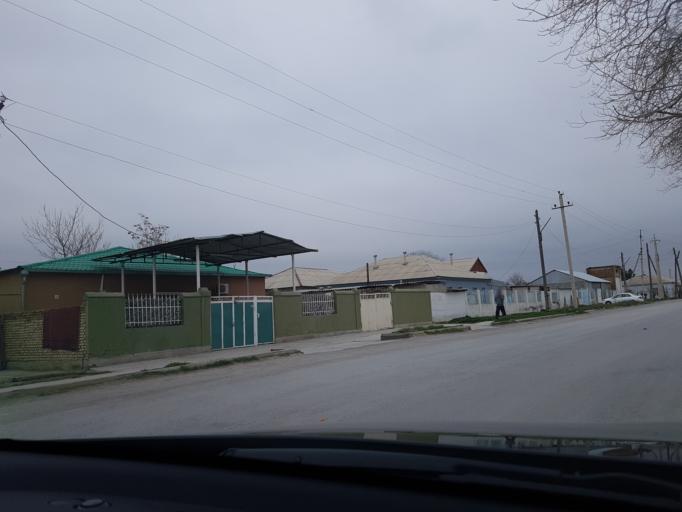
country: TM
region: Ahal
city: Abadan
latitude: 38.1557
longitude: 57.9641
